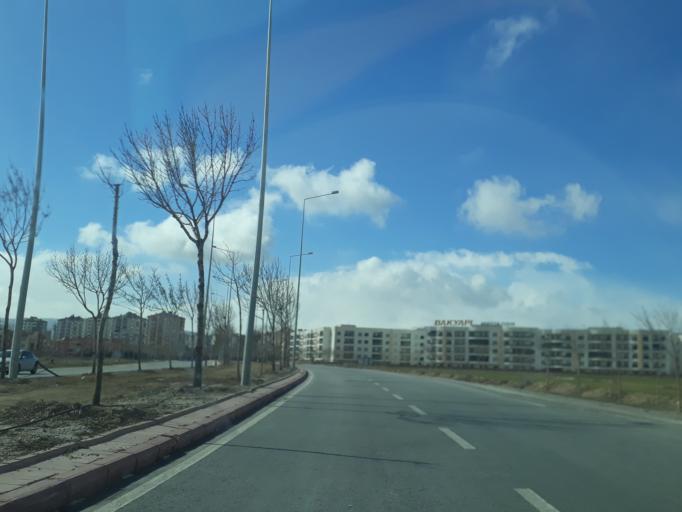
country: TR
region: Konya
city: Asagipinarbasi
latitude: 38.0066
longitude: 32.5414
